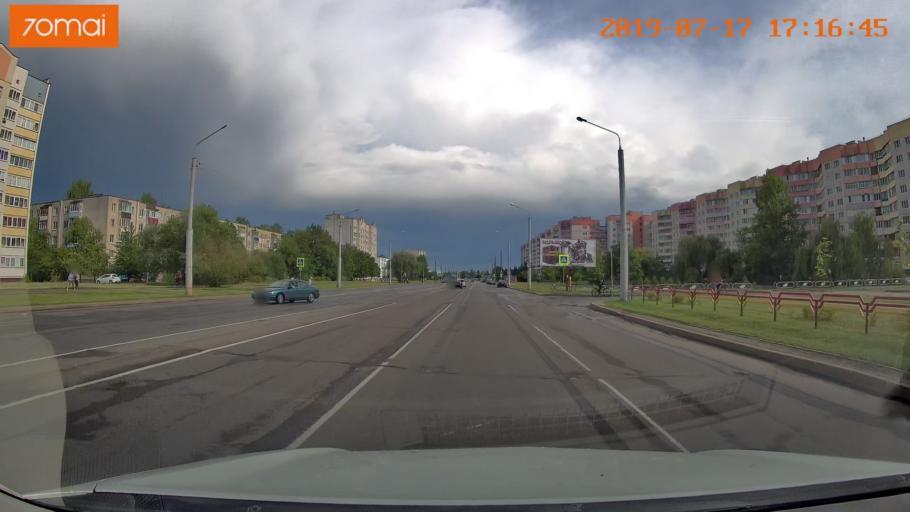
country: BY
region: Mogilev
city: Babruysk
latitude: 53.1655
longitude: 29.1952
